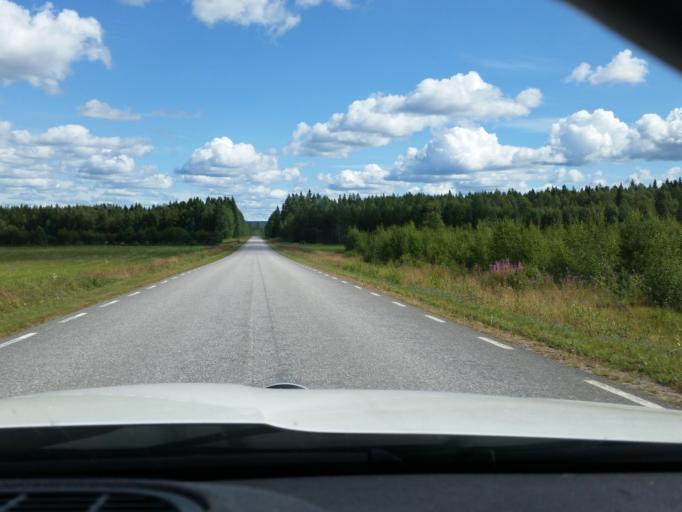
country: SE
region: Norrbotten
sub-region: Pitea Kommun
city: Roknas
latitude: 65.5045
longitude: 21.2439
